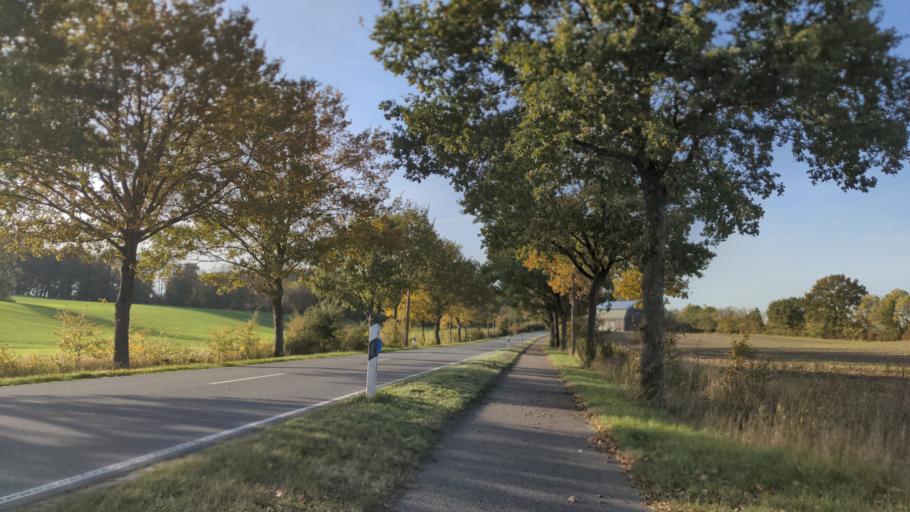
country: DE
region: Schleswig-Holstein
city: Kirchnuchel
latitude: 54.2019
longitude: 10.6861
